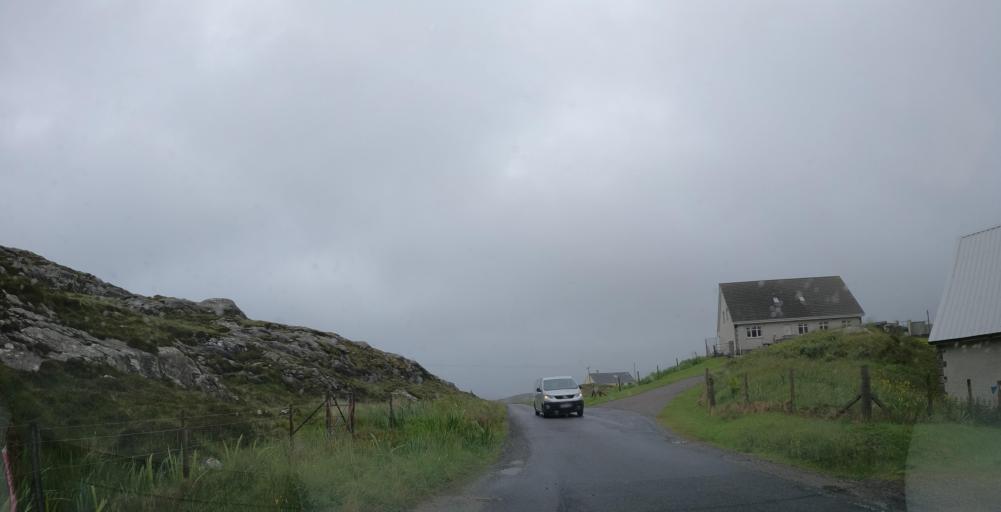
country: GB
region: Scotland
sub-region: Eilean Siar
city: Barra
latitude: 57.0120
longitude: -7.4320
